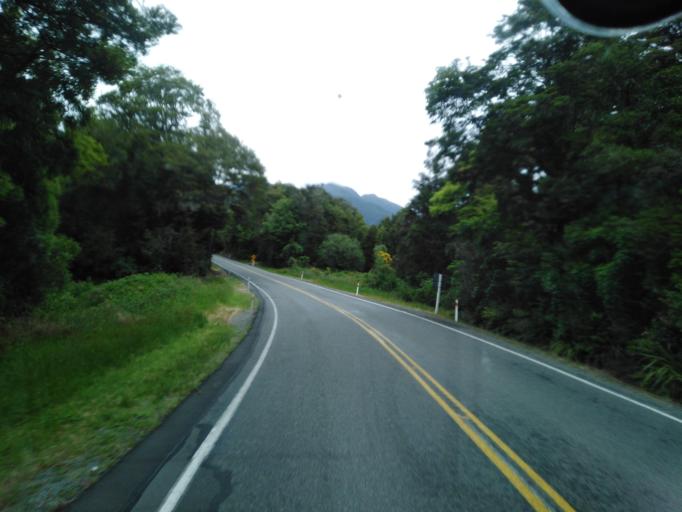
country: NZ
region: Tasman
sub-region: Tasman District
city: Wakefield
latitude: -41.7094
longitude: 172.5802
